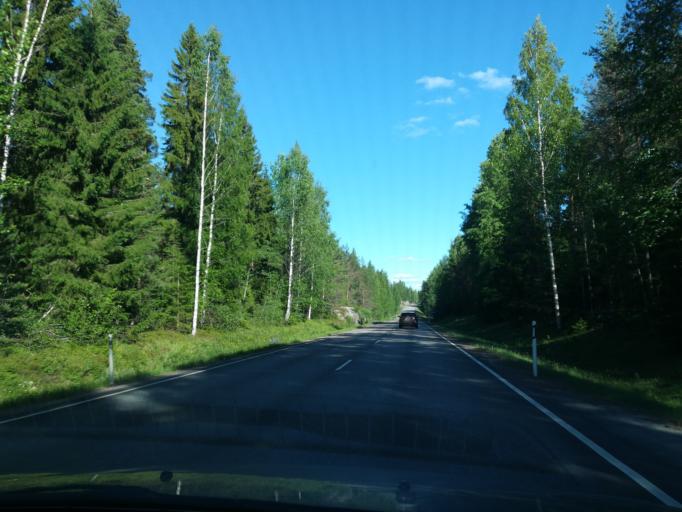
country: FI
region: South Karelia
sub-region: Imatra
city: Ruokolahti
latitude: 61.3651
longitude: 28.6891
